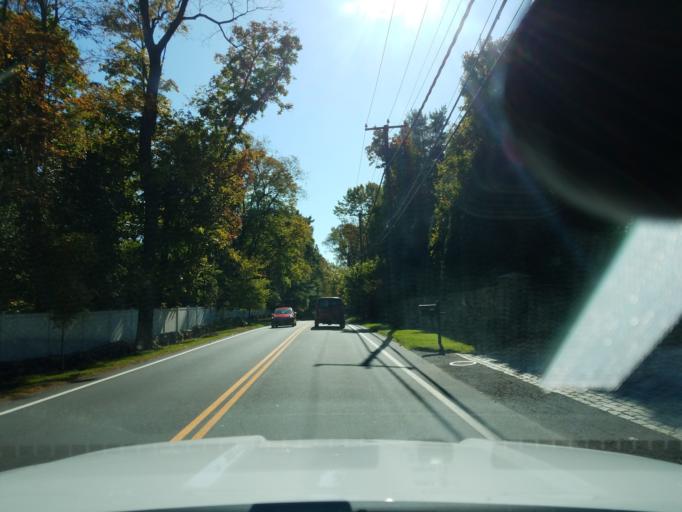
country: US
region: Connecticut
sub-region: Fairfield County
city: Glenville
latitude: 41.0885
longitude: -73.6298
